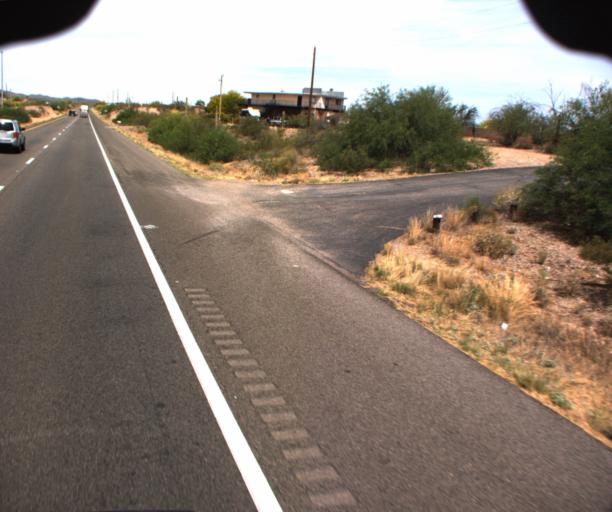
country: US
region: Arizona
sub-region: Maricopa County
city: Wickenburg
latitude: 33.8716
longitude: -112.6426
